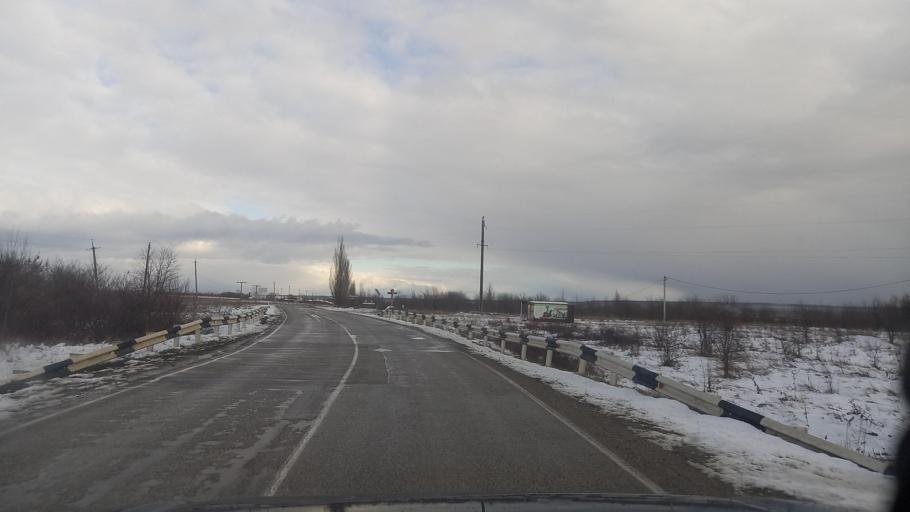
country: RU
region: Krasnodarskiy
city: Smolenskaya
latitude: 44.7724
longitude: 38.8216
